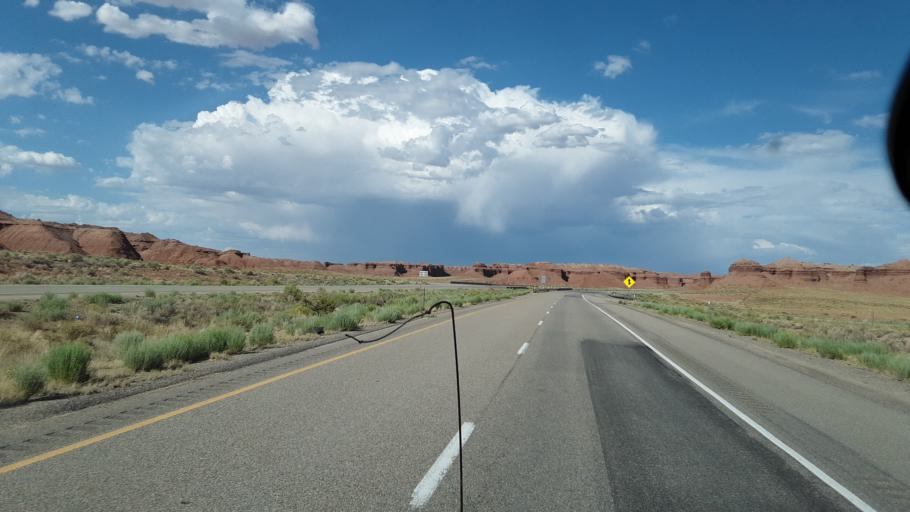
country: US
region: Utah
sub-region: Emery County
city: Ferron
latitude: 38.8431
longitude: -111.0591
